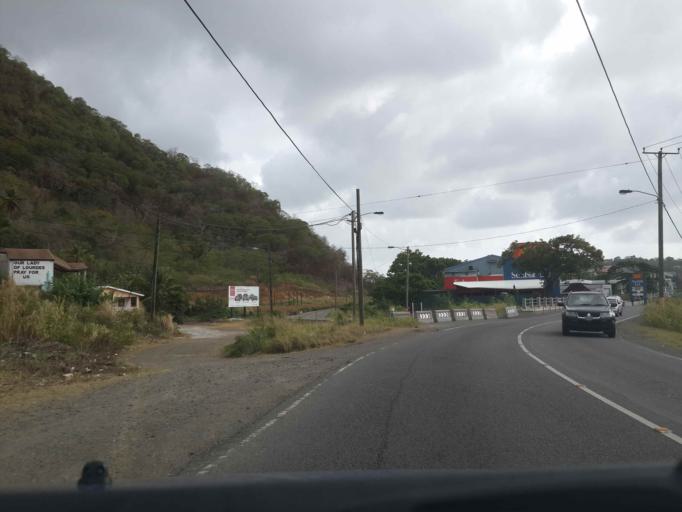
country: LC
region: Gros-Islet
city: Gros Islet
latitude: 14.0553
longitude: -60.9595
